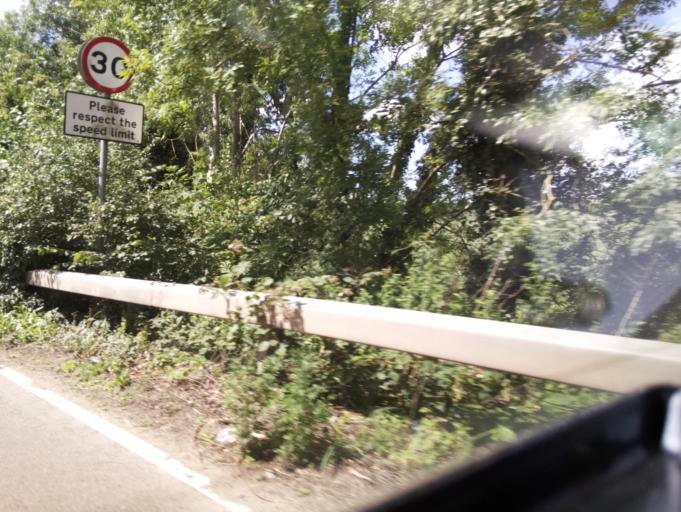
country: GB
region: England
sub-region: Nottinghamshire
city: Burton Joyce
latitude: 53.0028
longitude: -1.0518
